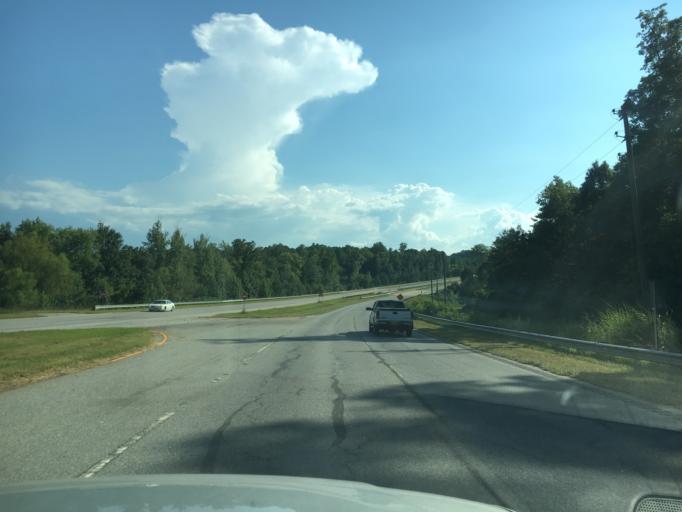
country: US
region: South Carolina
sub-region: Laurens County
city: Clinton
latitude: 34.4067
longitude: -81.9275
